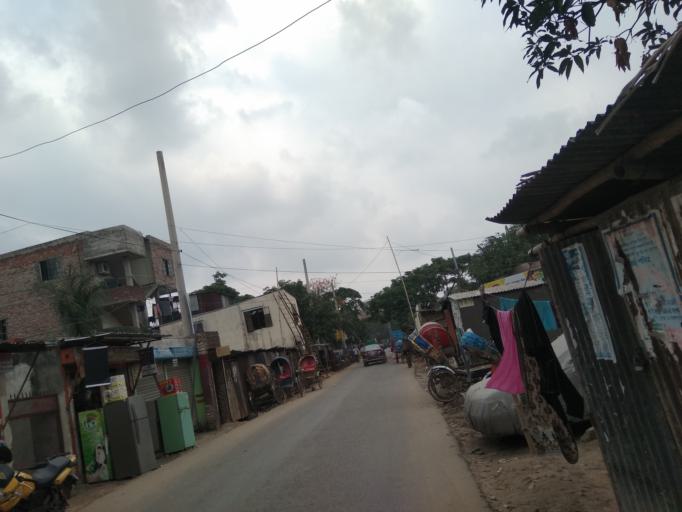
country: BD
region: Dhaka
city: Tungi
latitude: 23.8169
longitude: 90.3804
